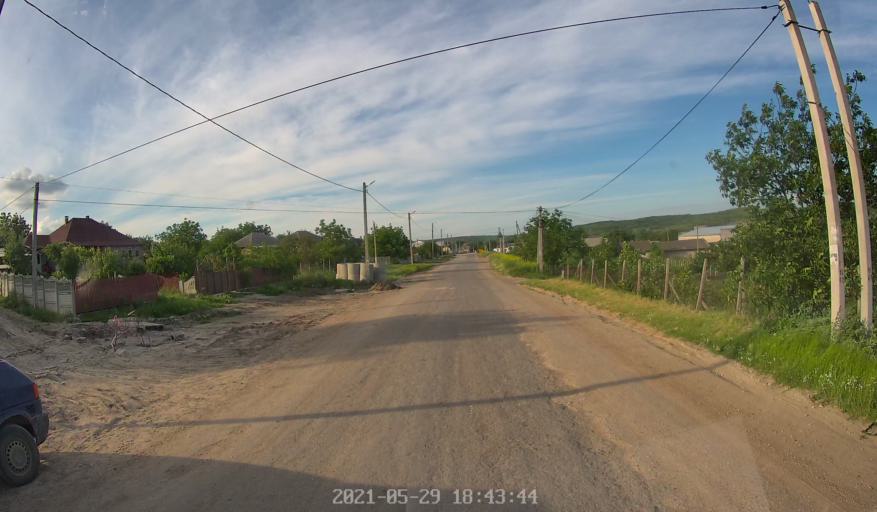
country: MD
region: Chisinau
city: Singera
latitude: 46.8202
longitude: 28.9659
